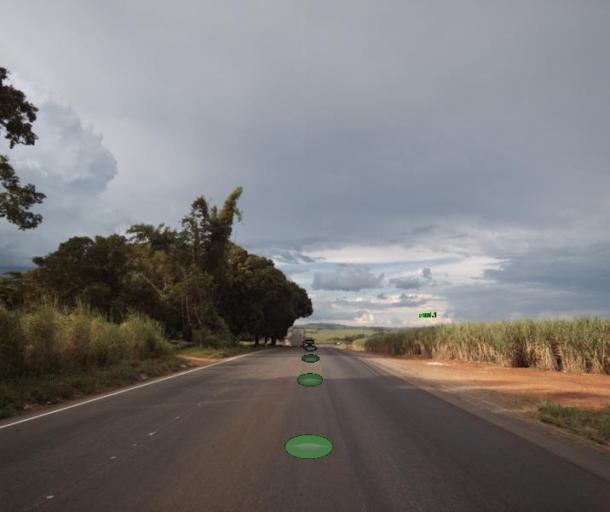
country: BR
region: Goias
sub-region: Ceres
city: Ceres
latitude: -15.1448
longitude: -49.5308
